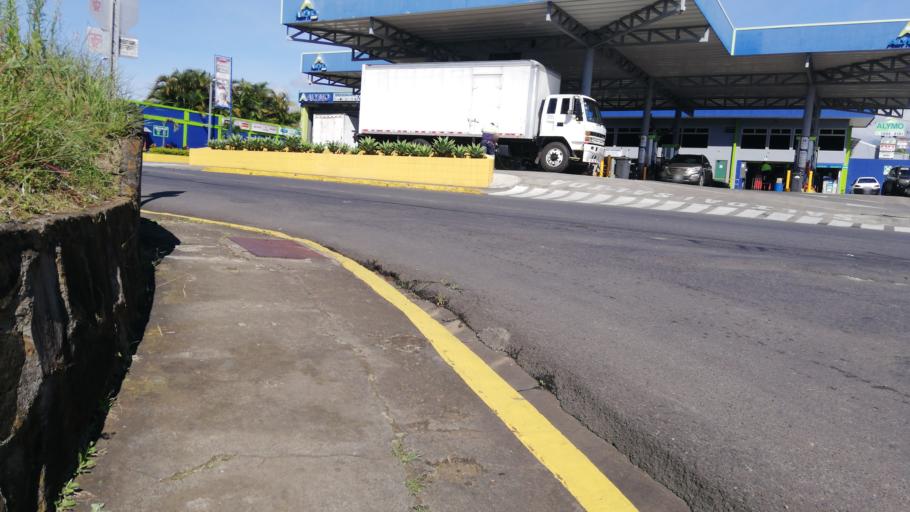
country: CR
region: Alajuela
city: San Juan
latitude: 10.0721
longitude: -84.3084
